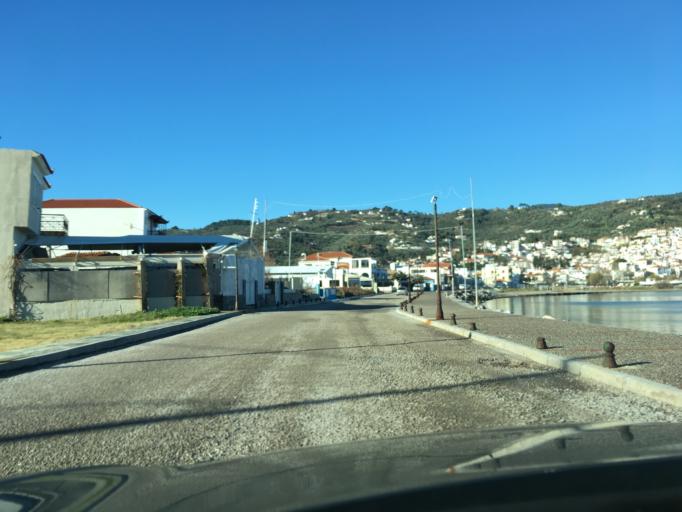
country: GR
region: Thessaly
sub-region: Nomos Magnisias
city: Skopelos
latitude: 39.1186
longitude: 23.7348
